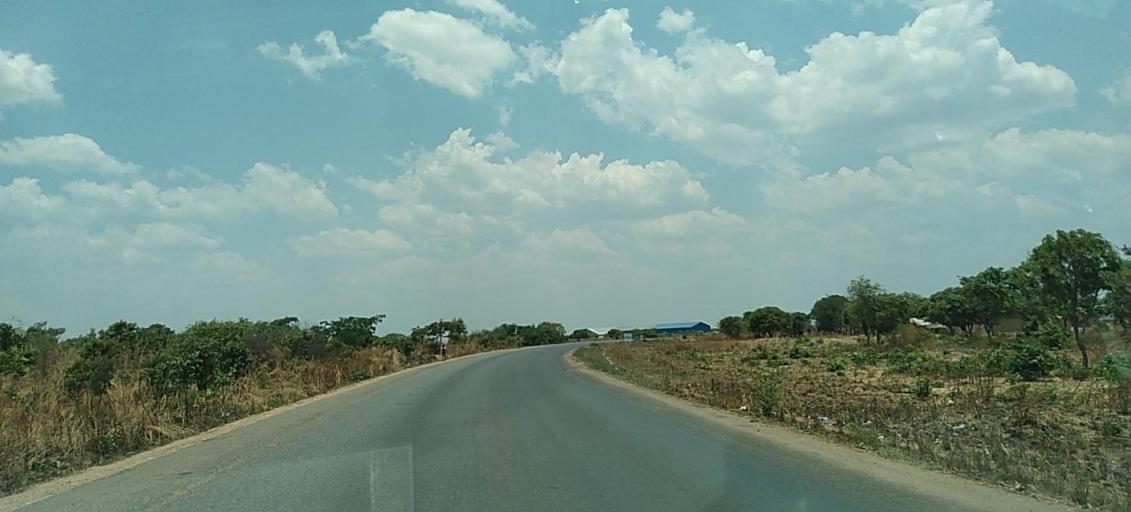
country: ZM
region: Central
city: Kapiri Mposhi
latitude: -13.8933
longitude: 28.6622
